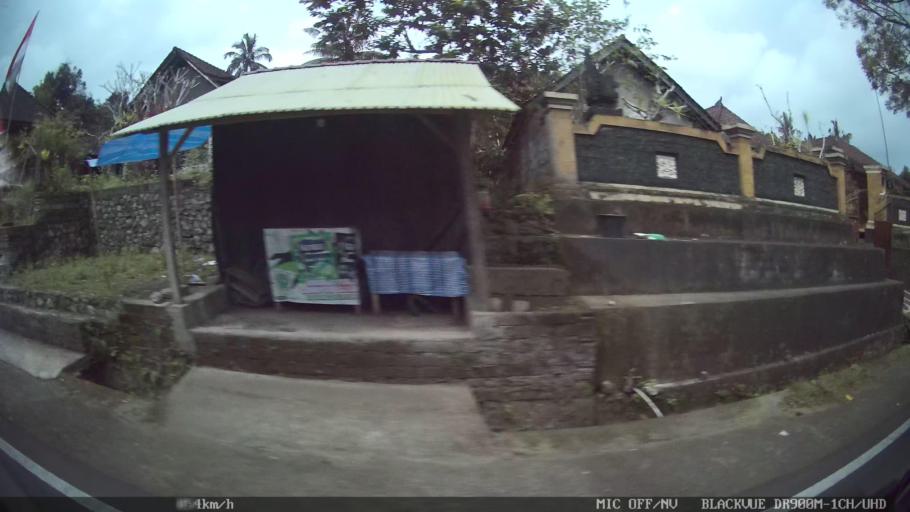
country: ID
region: Bali
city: Banjar Kubu
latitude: -8.3998
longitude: 115.4205
